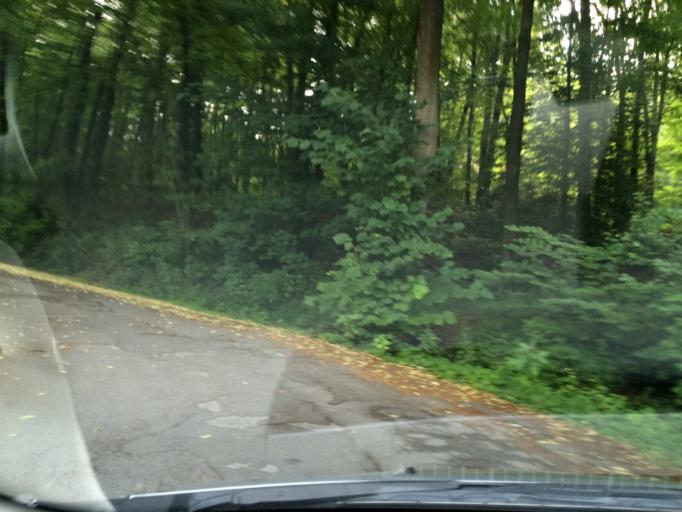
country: DE
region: North Rhine-Westphalia
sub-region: Regierungsbezirk Arnsberg
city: Nachrodt-Wiblingwerde
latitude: 51.3431
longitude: 7.5633
